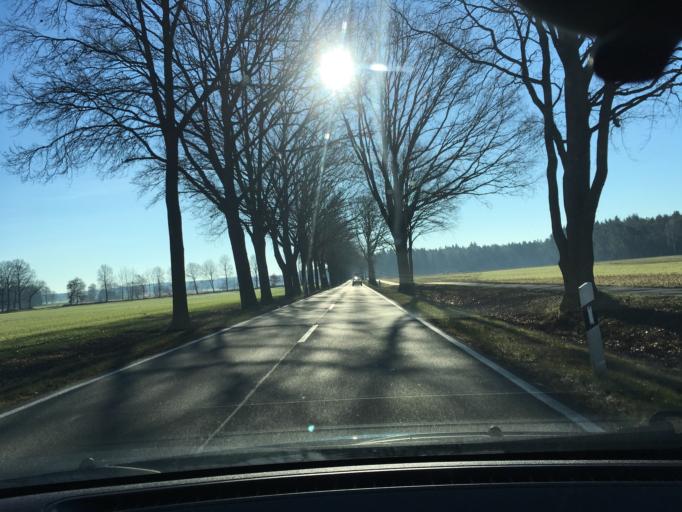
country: DE
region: Lower Saxony
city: Ebstorf
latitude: 53.0514
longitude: 10.4087
